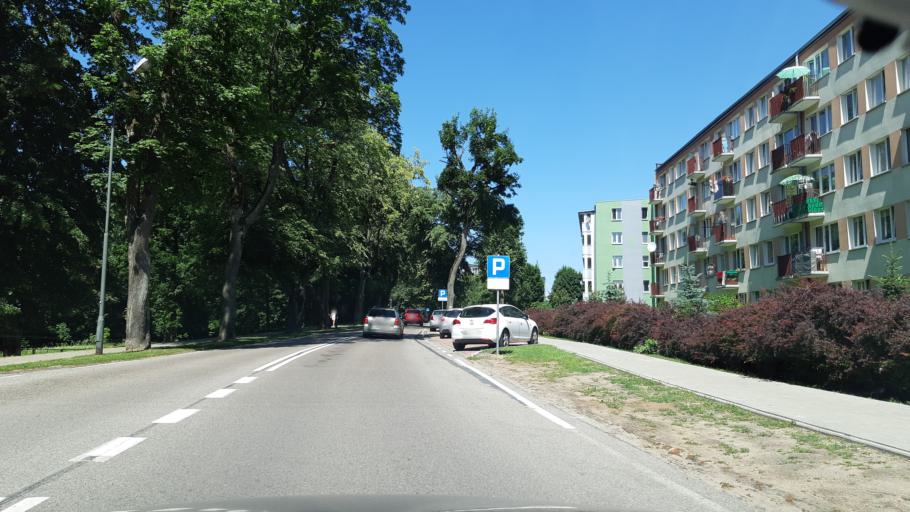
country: PL
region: Warmian-Masurian Voivodeship
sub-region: Powiat gizycki
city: Gizycko
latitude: 54.0355
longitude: 21.7538
